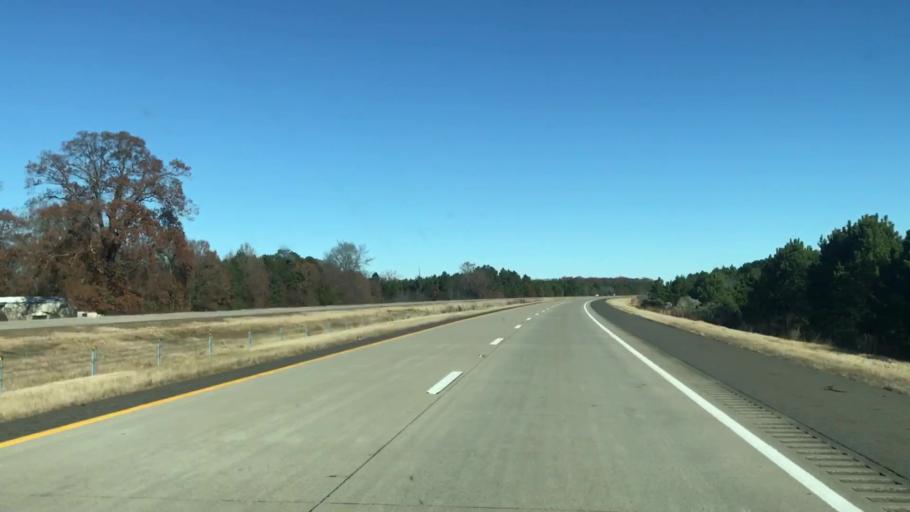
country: US
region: Texas
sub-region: Cass County
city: Queen City
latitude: 33.1989
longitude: -93.8773
